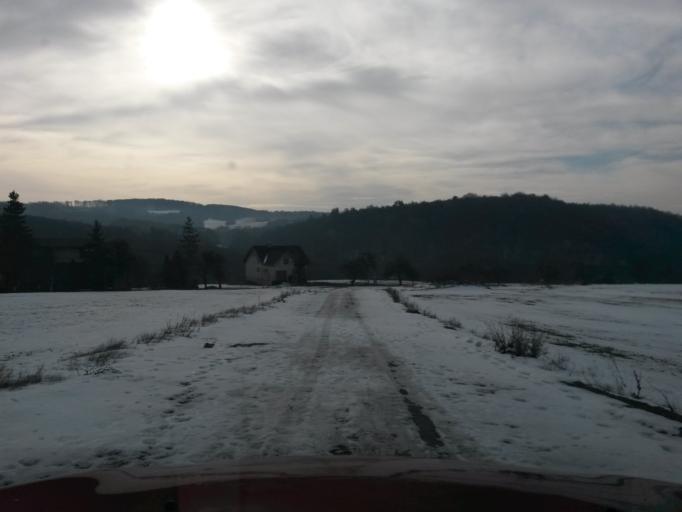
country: SK
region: Kosicky
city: Kosice
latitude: 48.7896
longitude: 21.3441
